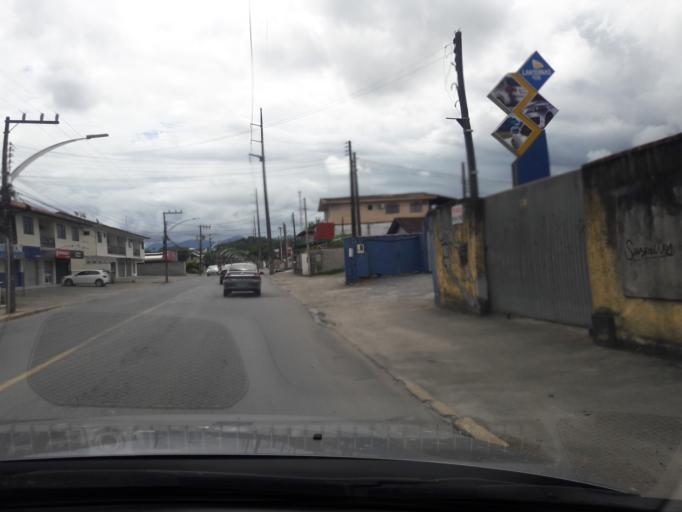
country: BR
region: Santa Catarina
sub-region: Joinville
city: Joinville
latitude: -26.3242
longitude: -48.8590
